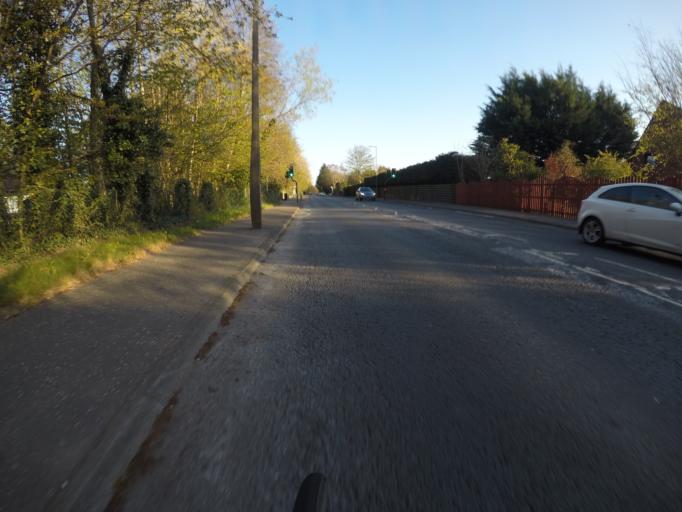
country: GB
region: Scotland
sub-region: North Ayrshire
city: Irvine
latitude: 55.6340
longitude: -4.6778
